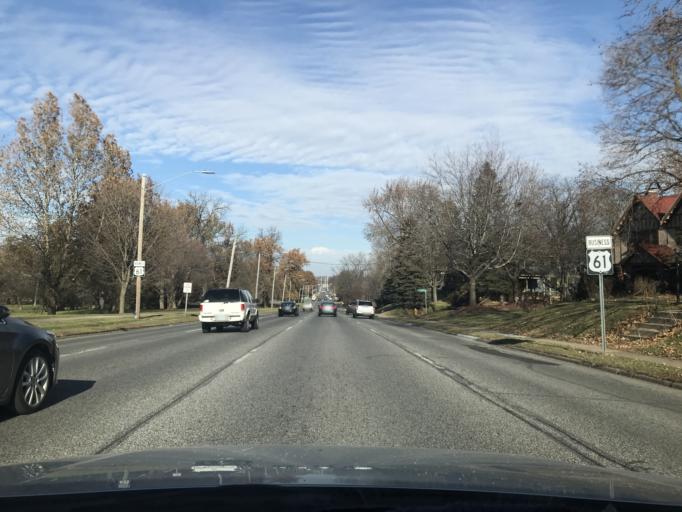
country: US
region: Iowa
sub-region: Scott County
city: Davenport
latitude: 41.5422
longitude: -90.5736
